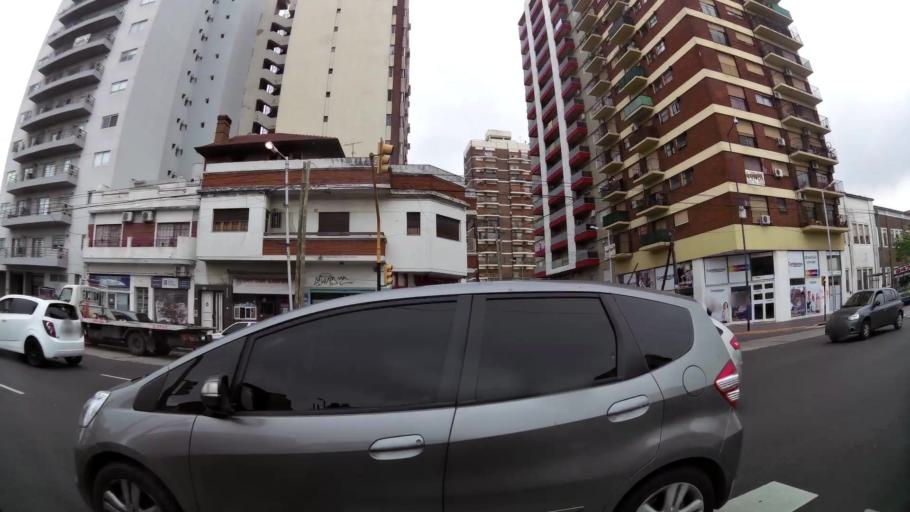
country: AR
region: Buenos Aires
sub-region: Partido de Avellaneda
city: Avellaneda
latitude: -34.6720
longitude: -58.3524
